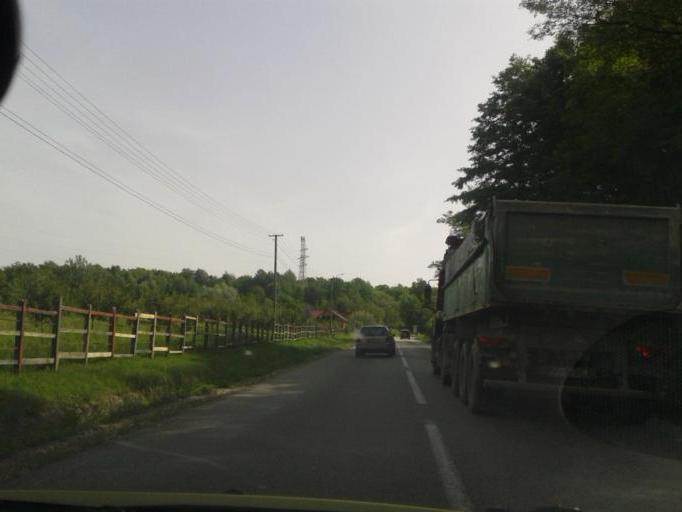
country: RO
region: Valcea
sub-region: Comuna Costesti
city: Costesti
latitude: 45.1398
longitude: 24.0715
